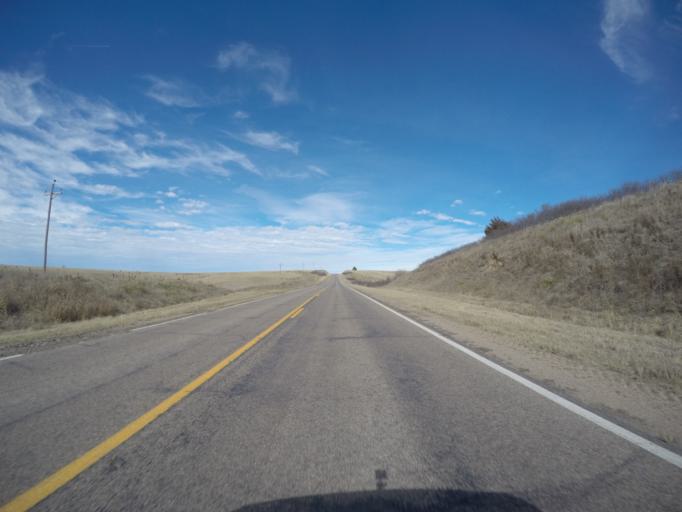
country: US
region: Nebraska
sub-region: Franklin County
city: Franklin
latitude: 40.1541
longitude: -98.9526
